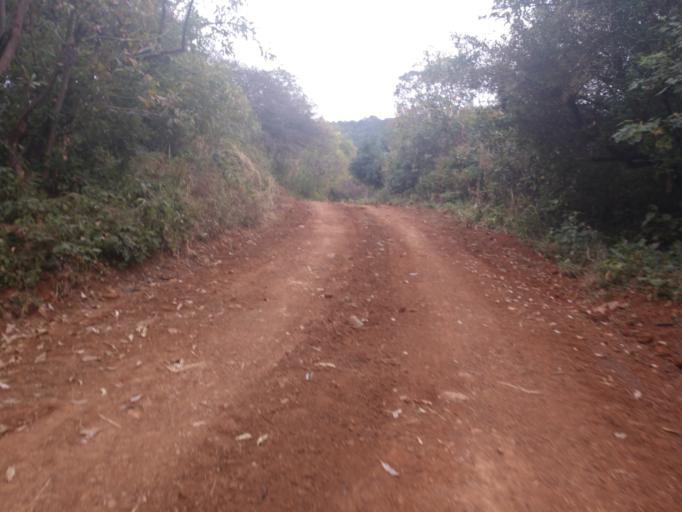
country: MX
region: Nayarit
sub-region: Tepic
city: La Corregidora
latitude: 21.4697
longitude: -104.7900
